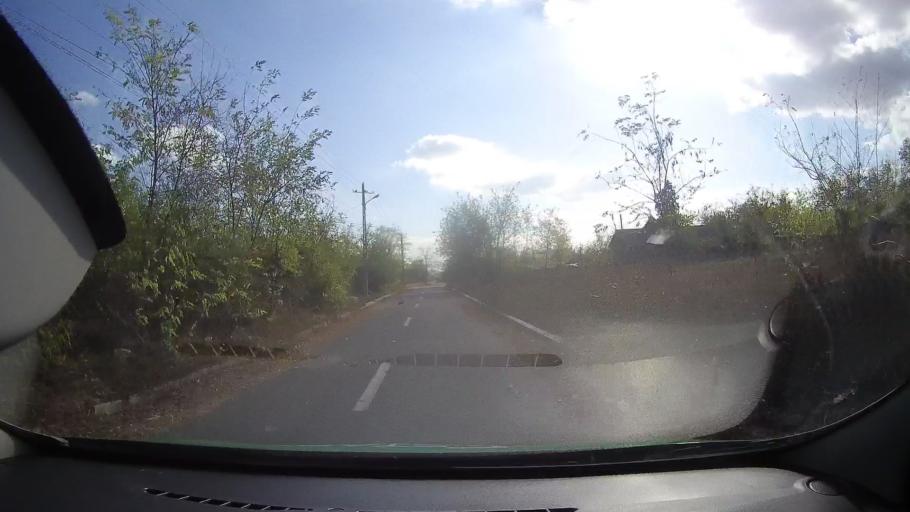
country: RO
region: Constanta
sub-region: Comuna Istria
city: Istria
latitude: 44.5768
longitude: 28.7124
